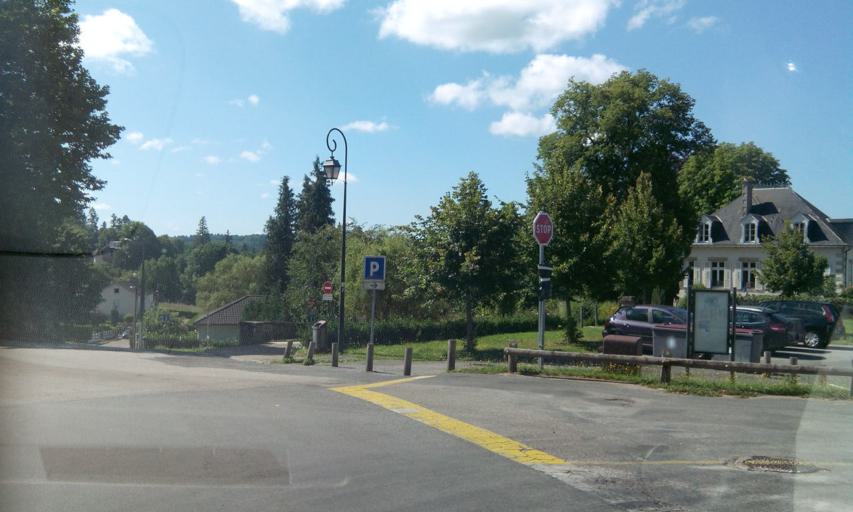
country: FR
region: Limousin
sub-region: Departement de la Haute-Vienne
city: Saint-Leonard-de-Noblat
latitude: 45.8374
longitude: 1.4870
